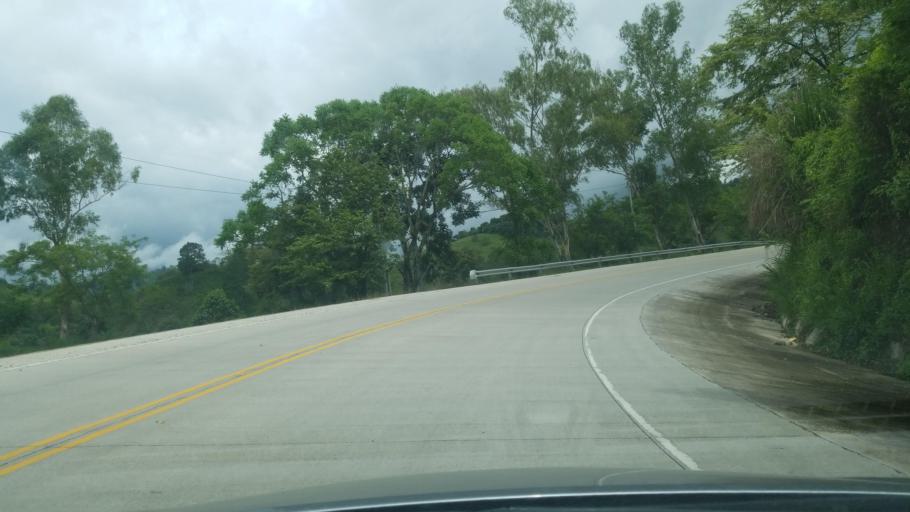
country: HN
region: Copan
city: San Jeronimo
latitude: 14.9610
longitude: -88.8935
